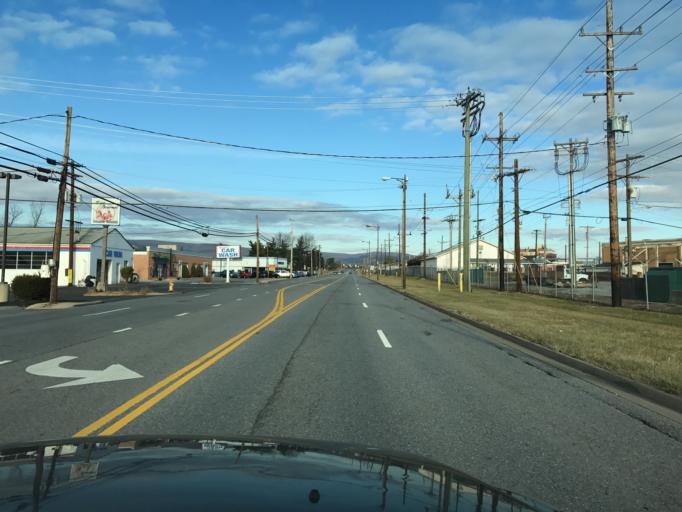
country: US
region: Maryland
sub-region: Frederick County
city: Frederick
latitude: 39.4290
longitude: -77.4325
